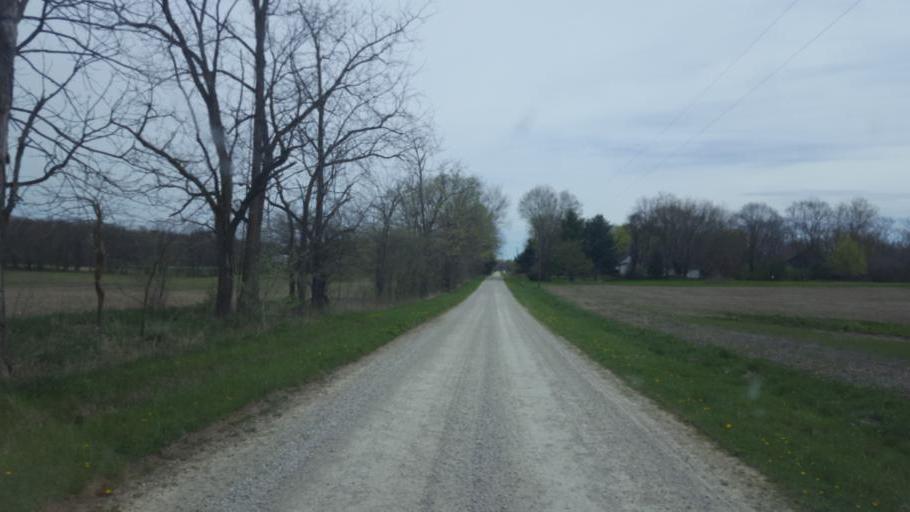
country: US
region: Ohio
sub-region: Knox County
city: Fredericktown
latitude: 40.5118
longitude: -82.6612
